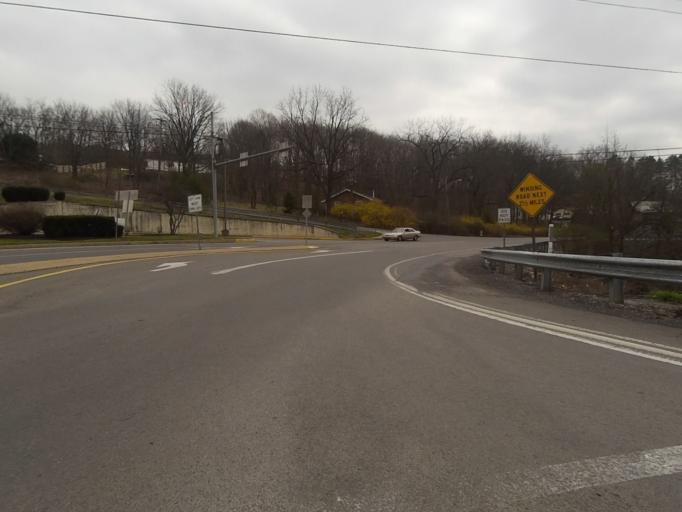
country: US
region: Pennsylvania
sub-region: Centre County
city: Lemont
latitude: 40.8181
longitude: -77.8185
